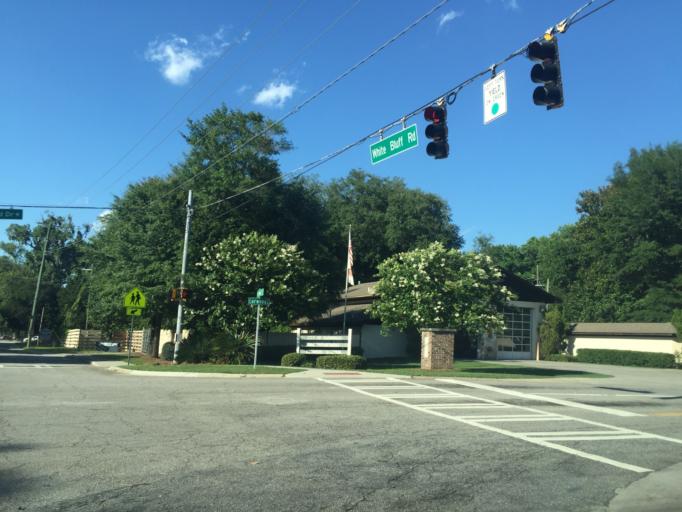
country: US
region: Georgia
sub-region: Chatham County
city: Montgomery
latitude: 31.9880
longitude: -81.1287
